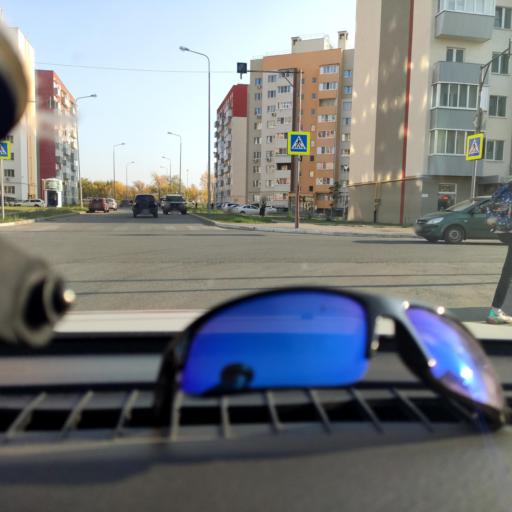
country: RU
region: Samara
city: Samara
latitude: 53.0948
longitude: 50.1646
